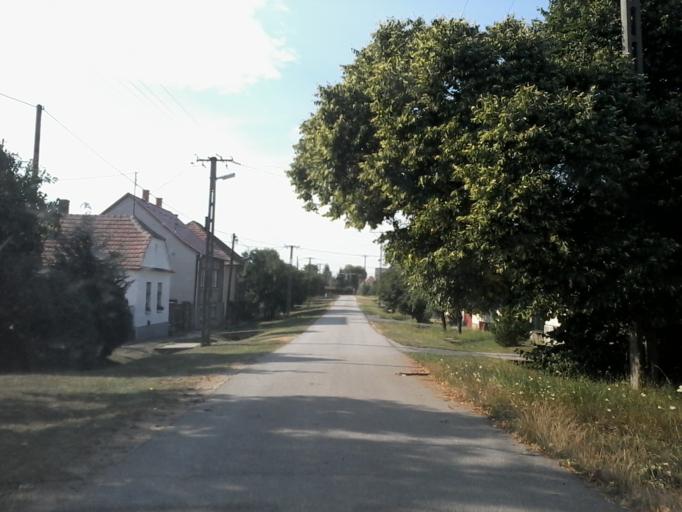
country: HU
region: Vas
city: Sarvar
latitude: 47.2174
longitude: 17.0050
